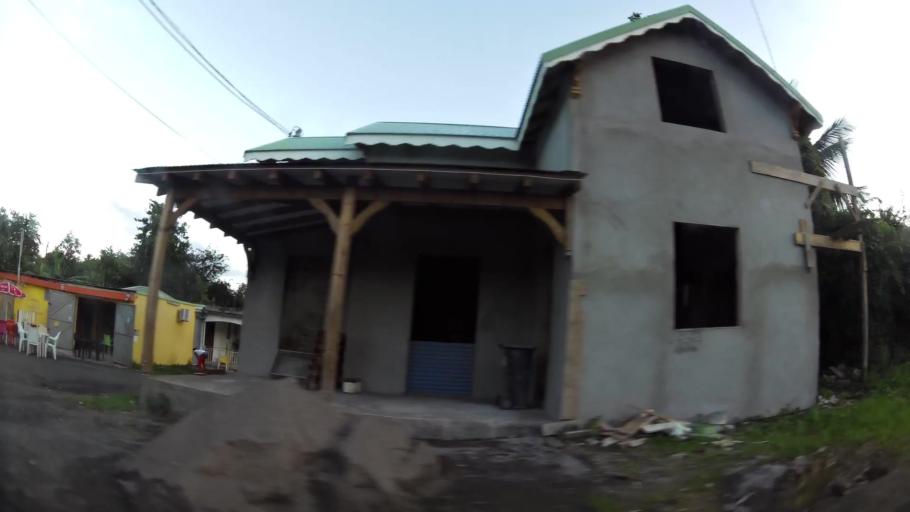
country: GP
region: Guadeloupe
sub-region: Guadeloupe
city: Les Abymes
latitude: 16.2681
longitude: -61.4973
